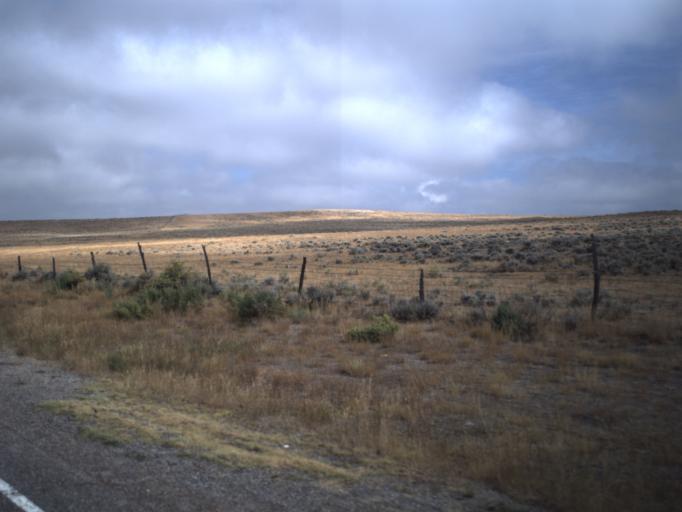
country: US
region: Utah
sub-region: Rich County
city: Randolph
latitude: 41.4737
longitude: -111.1099
